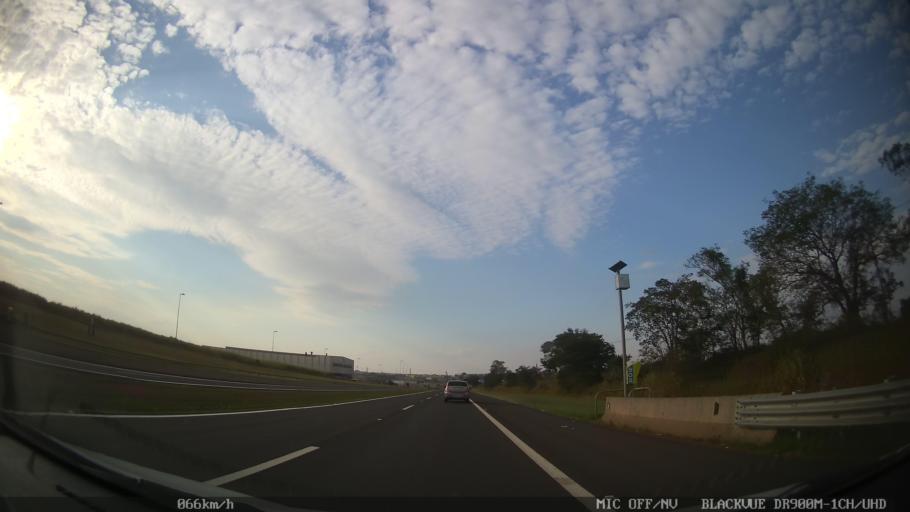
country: BR
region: Sao Paulo
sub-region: Artur Nogueira
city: Artur Nogueira
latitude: -22.6003
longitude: -47.1891
